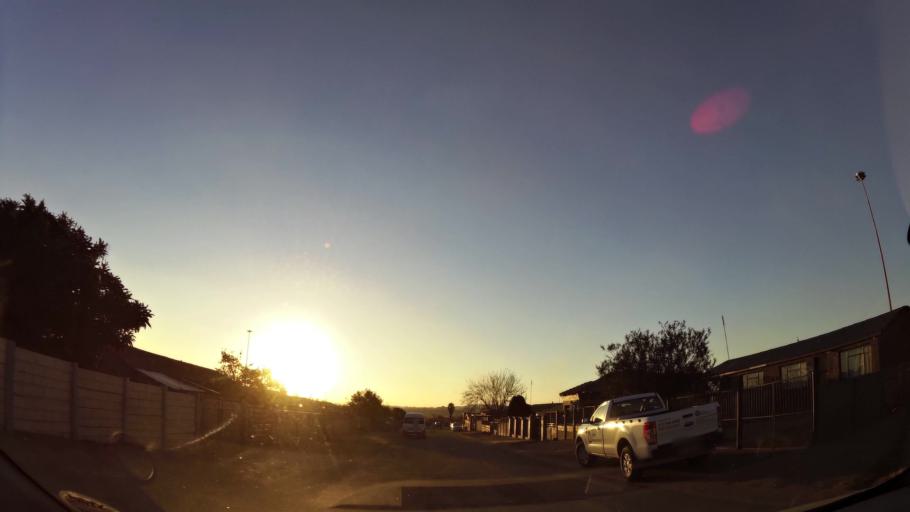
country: ZA
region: Mpumalanga
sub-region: Nkangala District Municipality
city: Witbank
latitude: -25.8878
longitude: 29.1816
